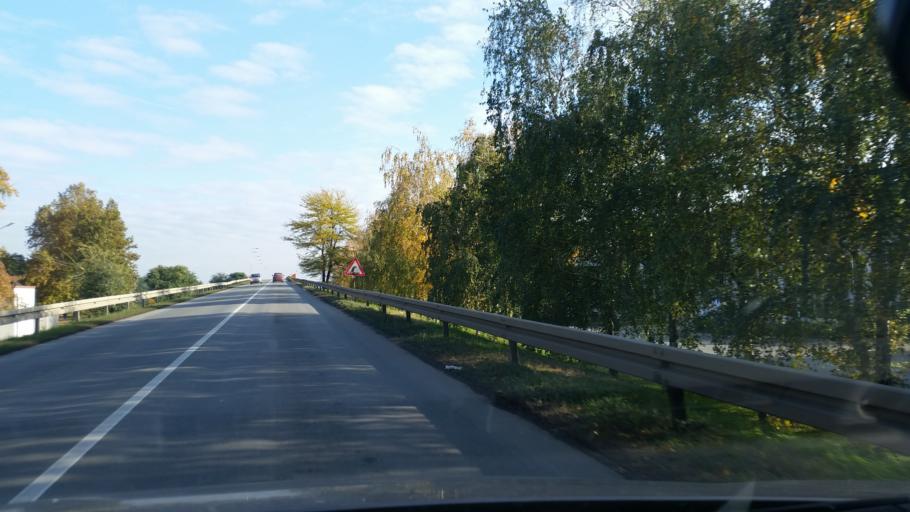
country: RS
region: Autonomna Pokrajina Vojvodina
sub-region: Srednjebanatski Okrug
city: Zrenjanin
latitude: 45.3720
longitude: 20.4166
